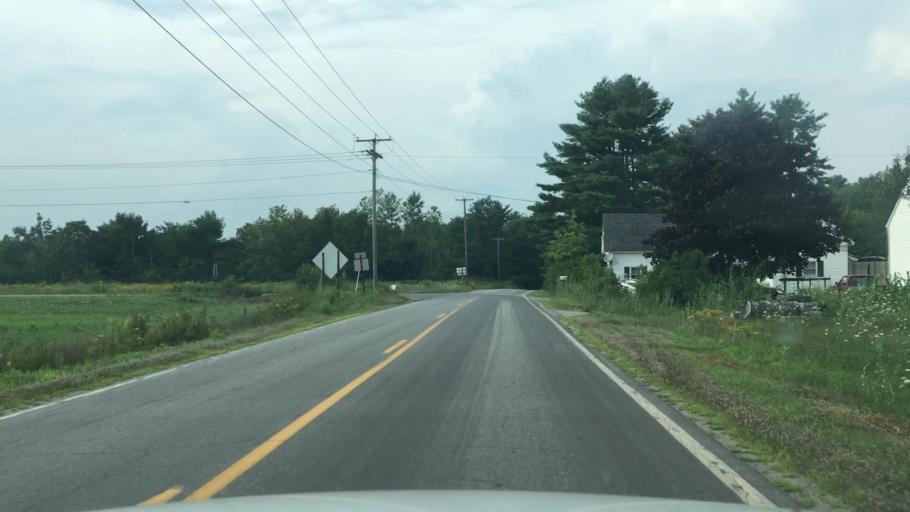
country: US
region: Maine
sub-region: Knox County
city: Washington
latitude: 44.2268
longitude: -69.3879
